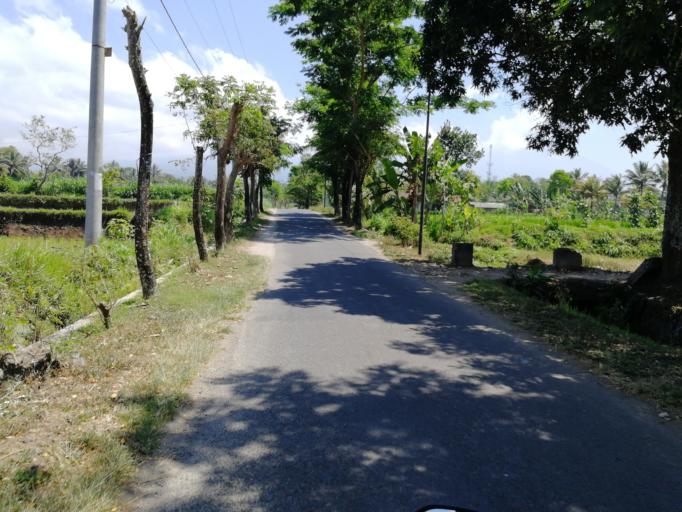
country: ID
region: West Nusa Tenggara
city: Tetebatu
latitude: -8.5577
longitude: 116.4195
